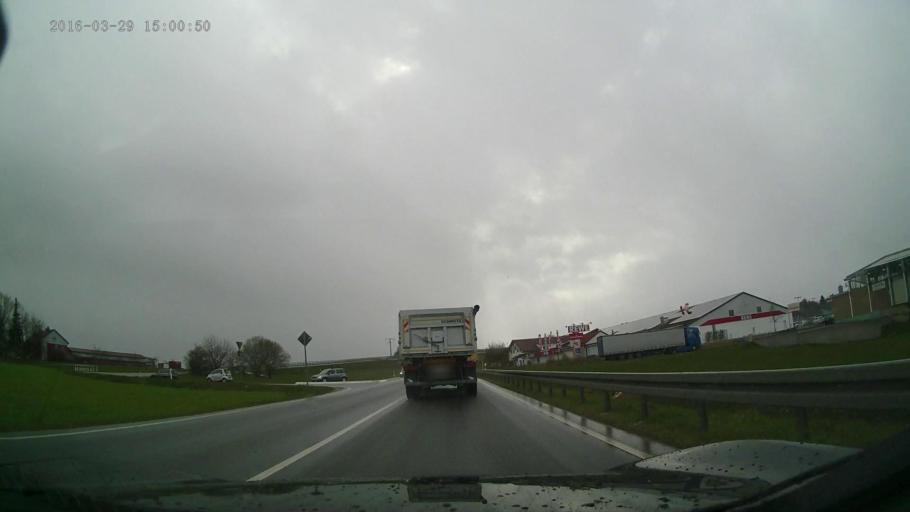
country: DE
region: Baden-Wuerttemberg
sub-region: Karlsruhe Region
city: Walldurn
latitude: 49.5757
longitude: 9.3713
